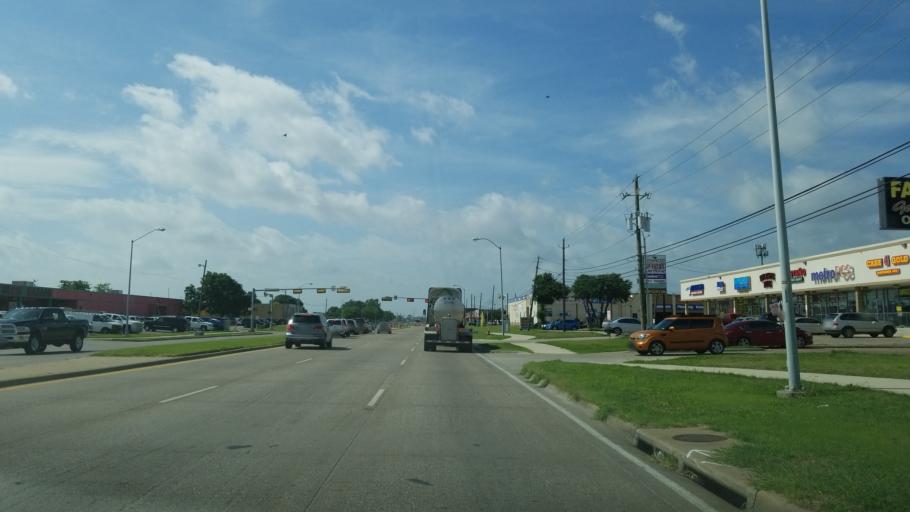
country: US
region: Texas
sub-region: Dallas County
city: Farmers Branch
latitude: 32.8750
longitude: -96.8841
